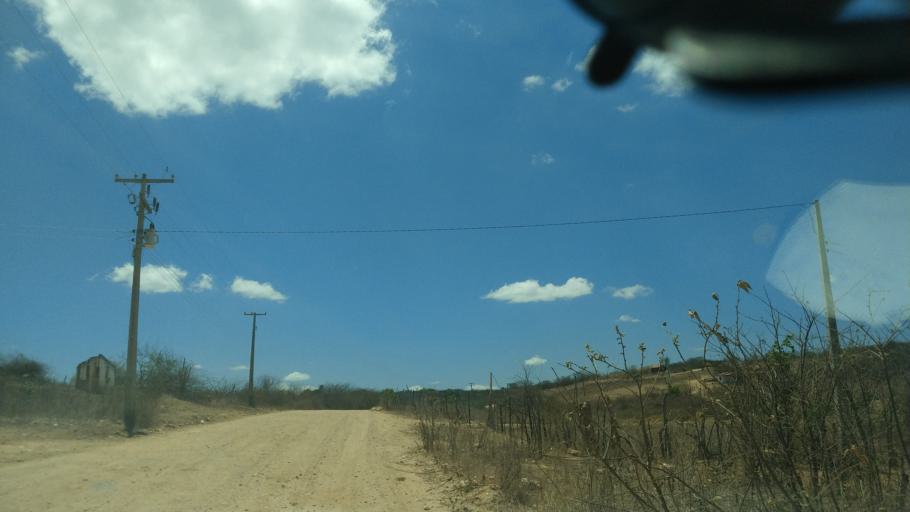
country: BR
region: Rio Grande do Norte
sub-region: Cerro Cora
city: Cerro Cora
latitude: -6.0215
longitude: -36.3319
